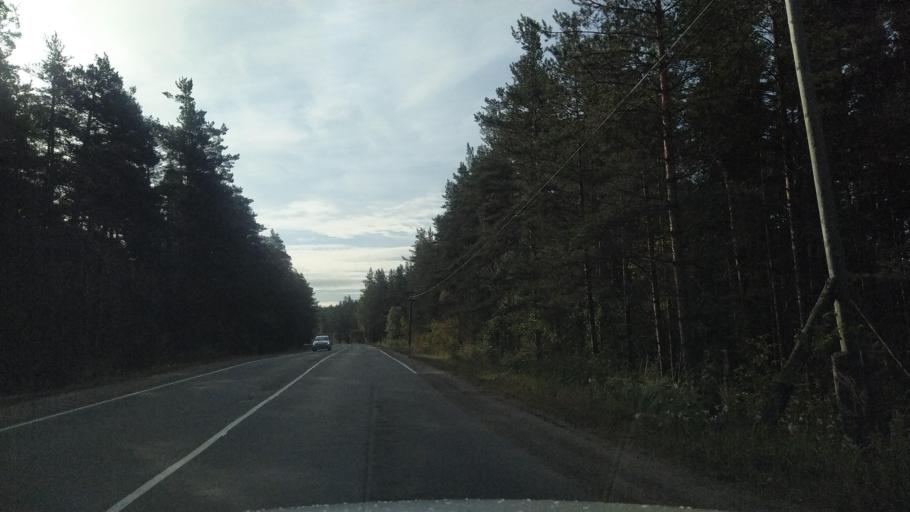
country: RU
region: Leningrad
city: Priozersk
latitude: 61.0029
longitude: 30.1923
